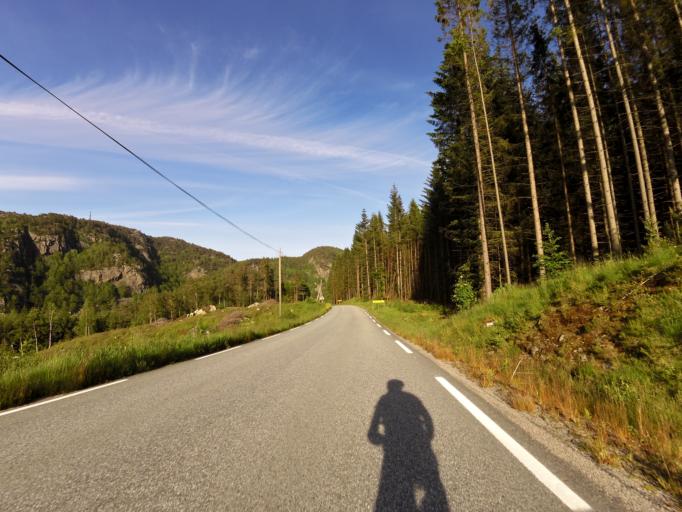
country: NO
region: Vest-Agder
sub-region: Flekkefjord
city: Flekkefjord
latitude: 58.2861
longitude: 6.6059
